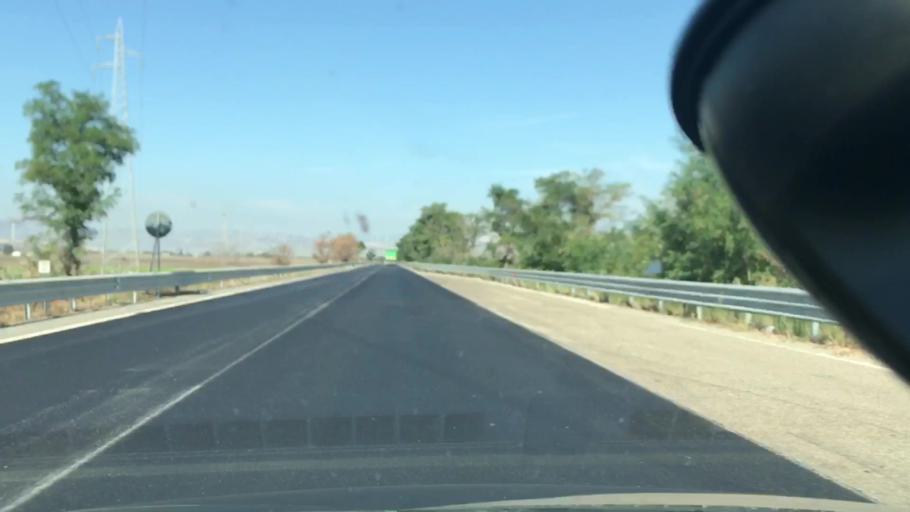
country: IT
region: Basilicate
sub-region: Provincia di Potenza
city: Zona 179
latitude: 41.0770
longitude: 15.6387
